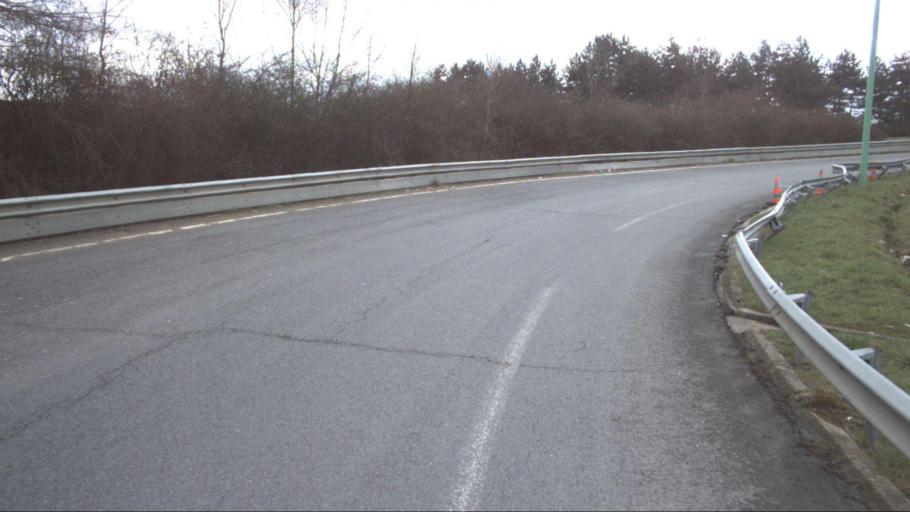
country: FR
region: Ile-de-France
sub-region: Departement des Yvelines
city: Saint-Cyr-l'Ecole
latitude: 48.7891
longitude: 2.0628
